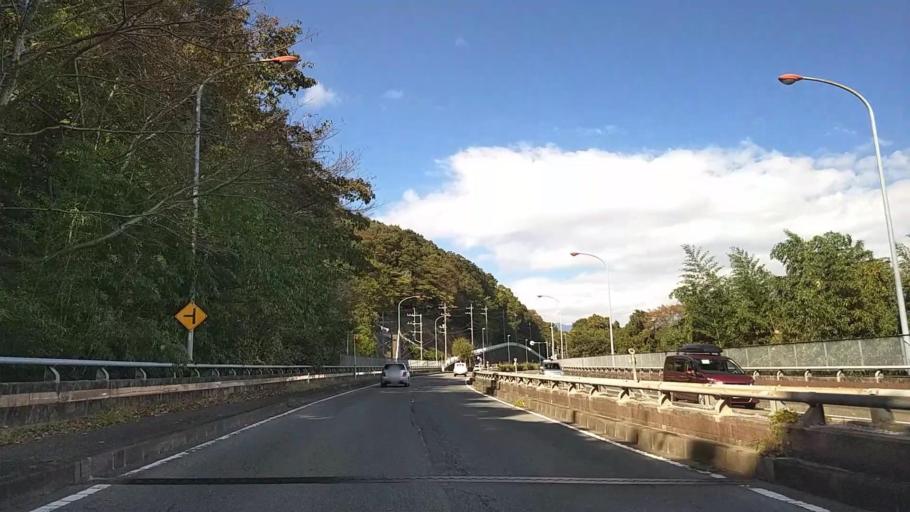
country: JP
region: Kanagawa
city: Ninomiya
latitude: 35.3278
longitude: 139.2334
